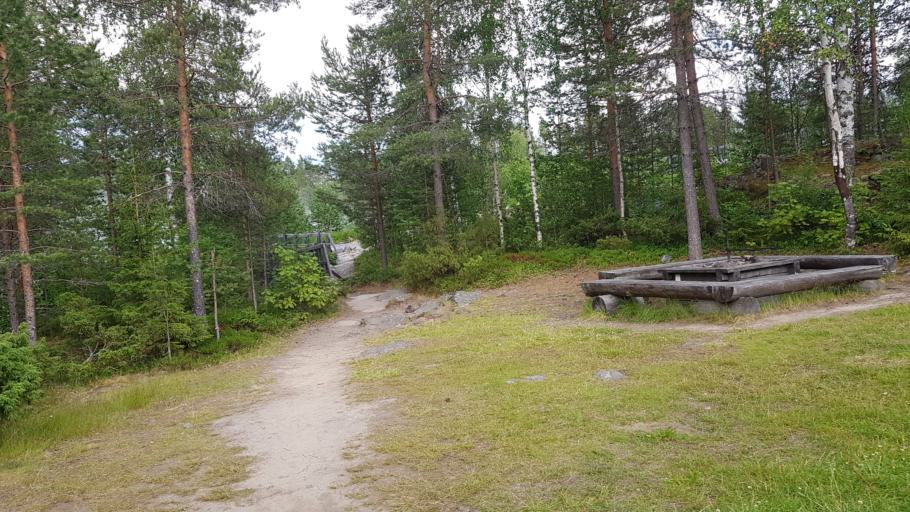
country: SE
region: Norrbotten
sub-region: Alvsbyns Kommun
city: AElvsbyn
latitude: 65.8514
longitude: 20.4066
